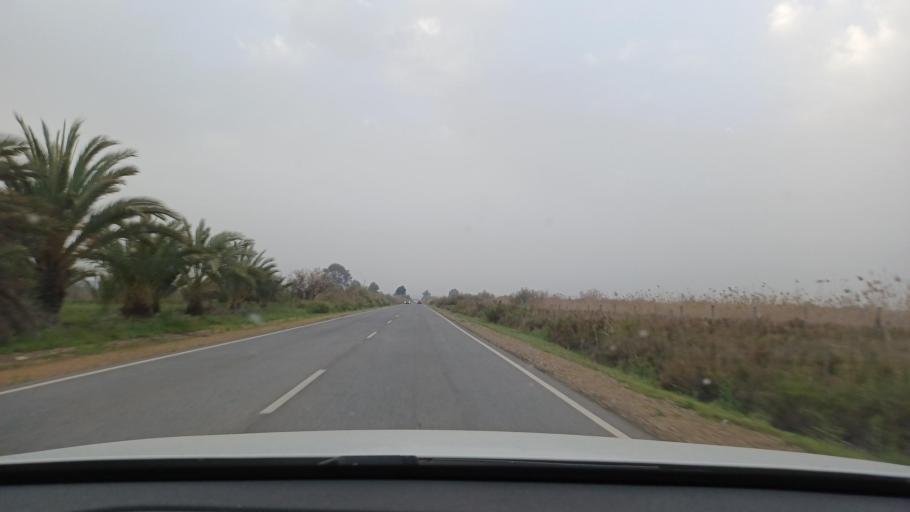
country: ES
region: Valencia
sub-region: Provincia de Alicante
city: Dolores
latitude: 38.1745
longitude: -0.7021
